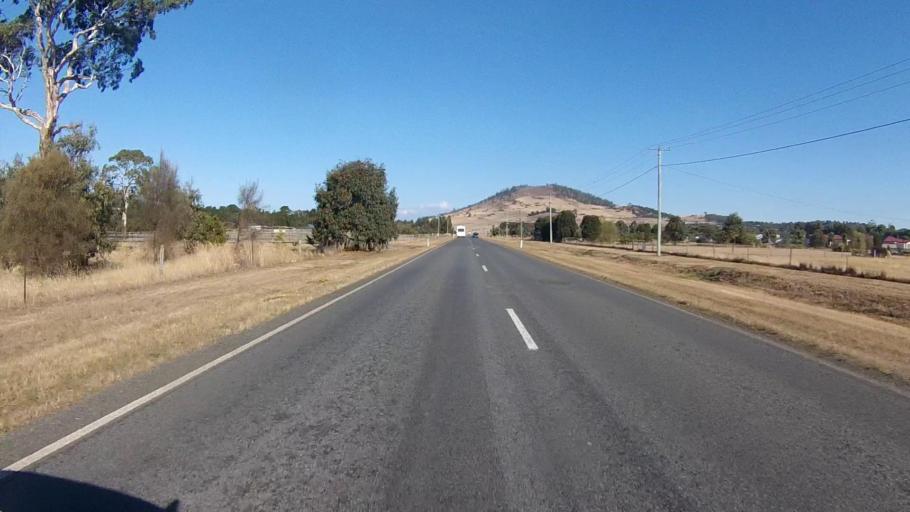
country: AU
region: Tasmania
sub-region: Clarence
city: Seven Mile Beach
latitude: -42.8556
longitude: 147.4890
